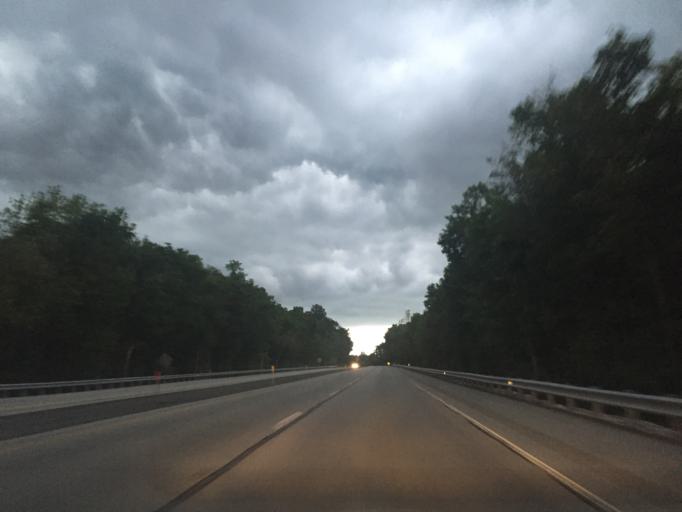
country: US
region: Pennsylvania
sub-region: York County
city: Grantley
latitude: 39.9384
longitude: -76.7138
